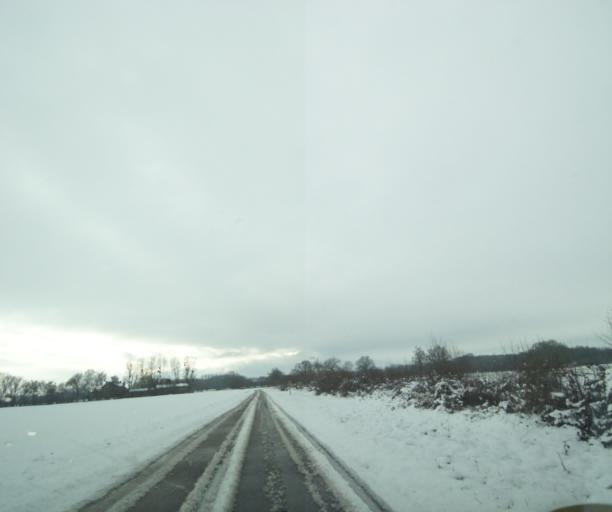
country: FR
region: Champagne-Ardenne
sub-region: Departement de la Haute-Marne
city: Montier-en-Der
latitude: 48.4729
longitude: 4.6641
